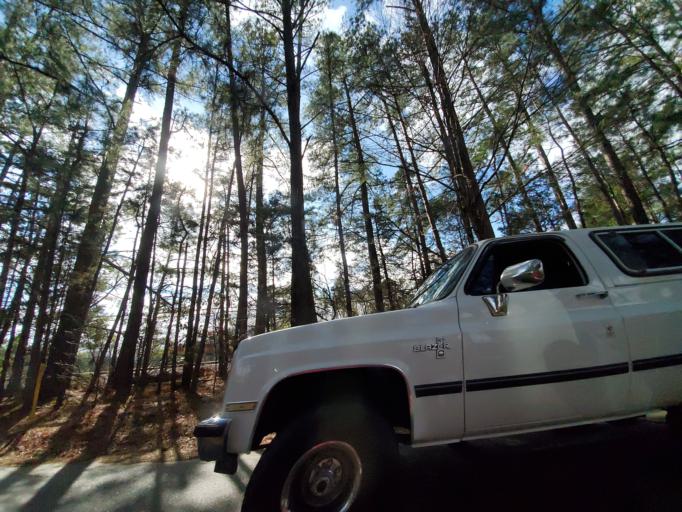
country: US
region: Georgia
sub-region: Clarke County
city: Country Club Estates
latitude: 33.9984
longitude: -83.4426
